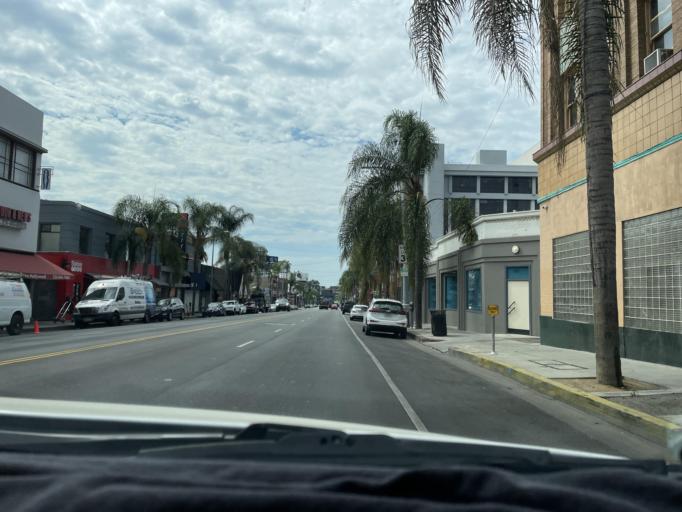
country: US
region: California
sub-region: Kern County
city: Tehachapi
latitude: 35.1385
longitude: -118.3202
